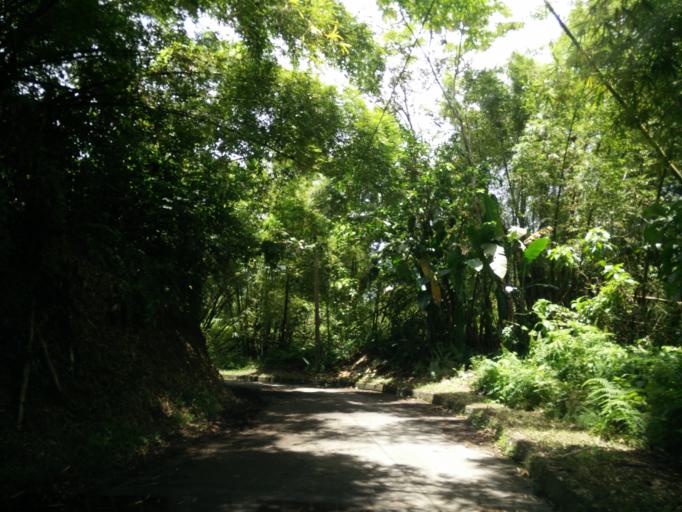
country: MQ
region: Martinique
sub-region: Martinique
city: Le Morne-Rouge
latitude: 14.7828
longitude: -61.1424
